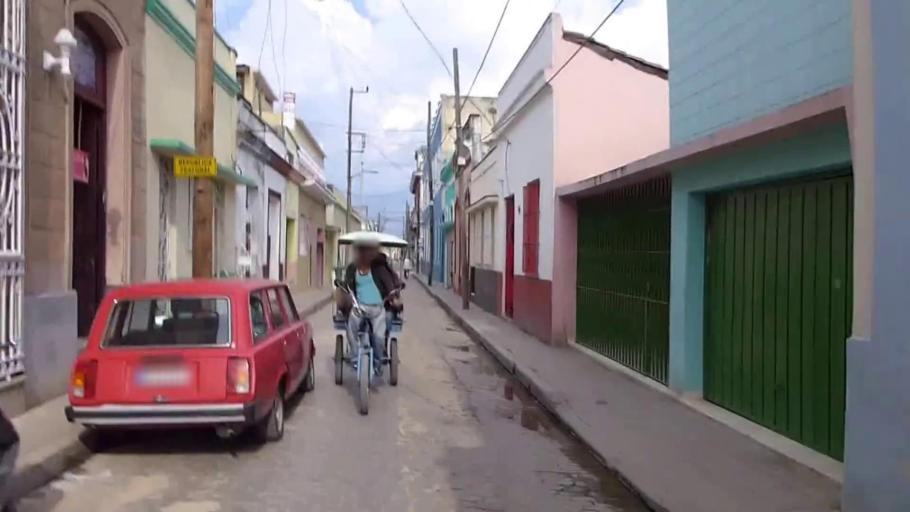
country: CU
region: Camaguey
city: Camaguey
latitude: 21.3866
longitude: -77.9174
